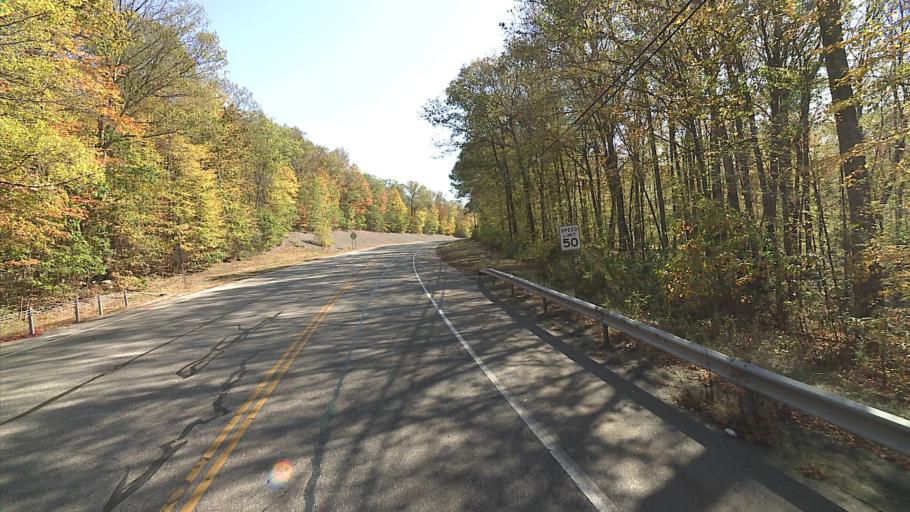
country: US
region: Connecticut
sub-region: Windham County
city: Windham
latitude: 41.7756
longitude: -72.0724
